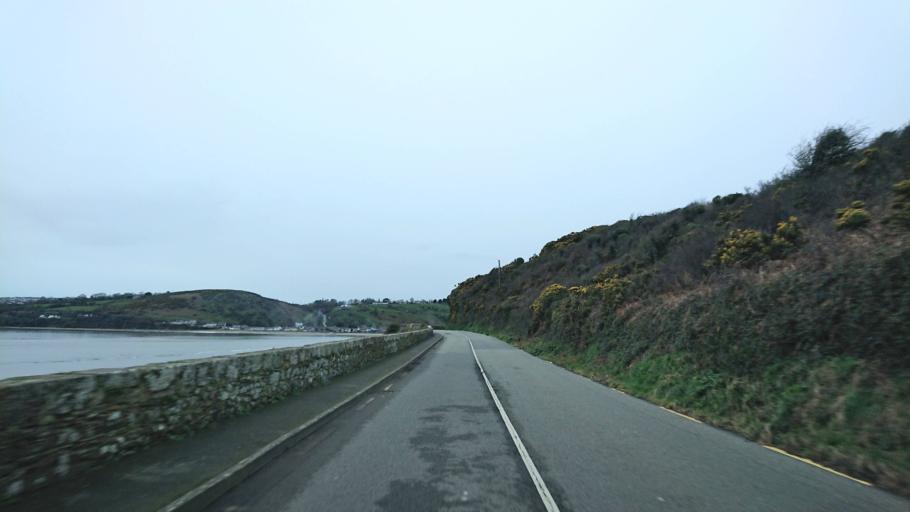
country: IE
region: Munster
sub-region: Waterford
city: Dunmore East
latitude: 52.2422
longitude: -6.9588
